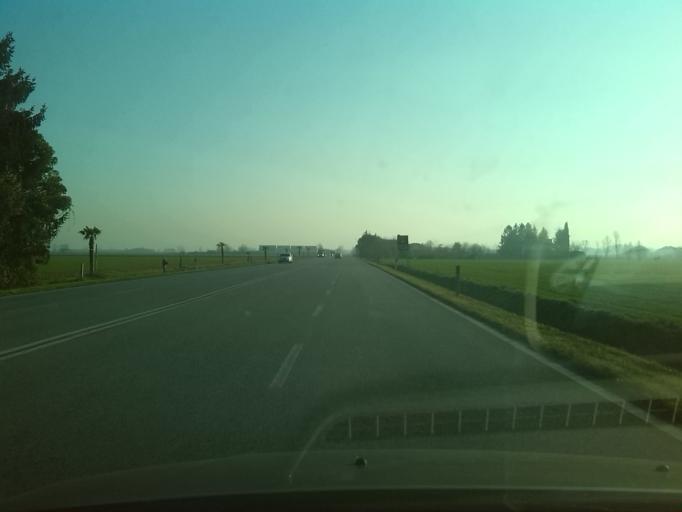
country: IT
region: Friuli Venezia Giulia
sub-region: Provincia di Udine
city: Pertegada
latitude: 45.7371
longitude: 13.0408
